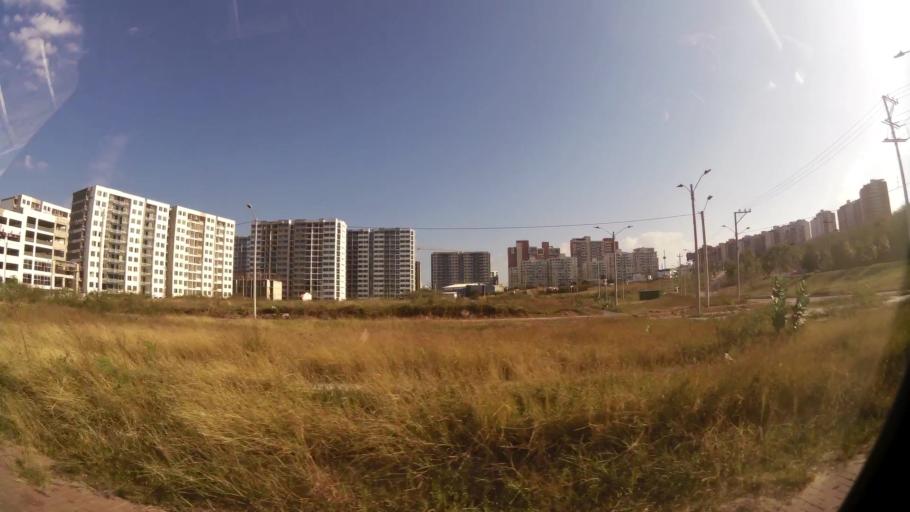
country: CO
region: Atlantico
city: Barranquilla
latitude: 11.0051
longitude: -74.8381
